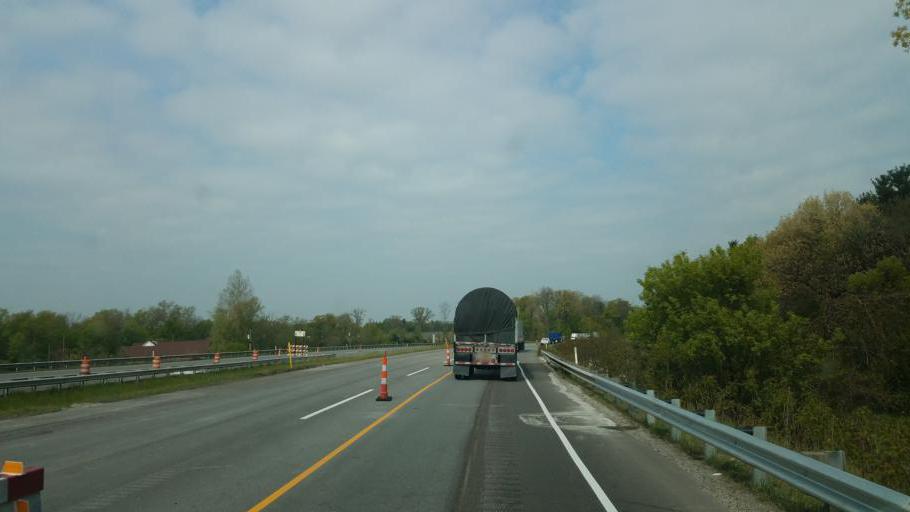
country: US
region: Indiana
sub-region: Saint Joseph County
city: Georgetown
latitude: 41.7169
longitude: -86.2364
